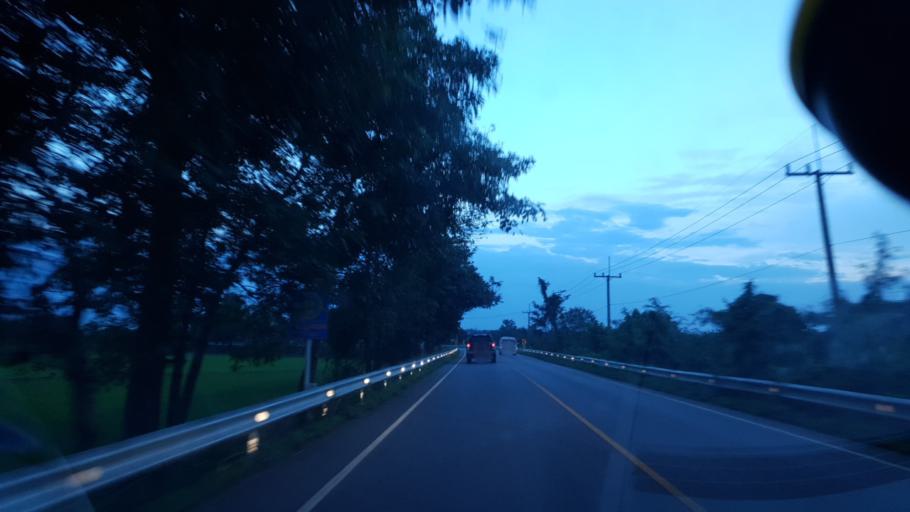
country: TH
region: Chiang Rai
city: Wiang Chiang Rung
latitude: 19.9688
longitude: 99.9810
